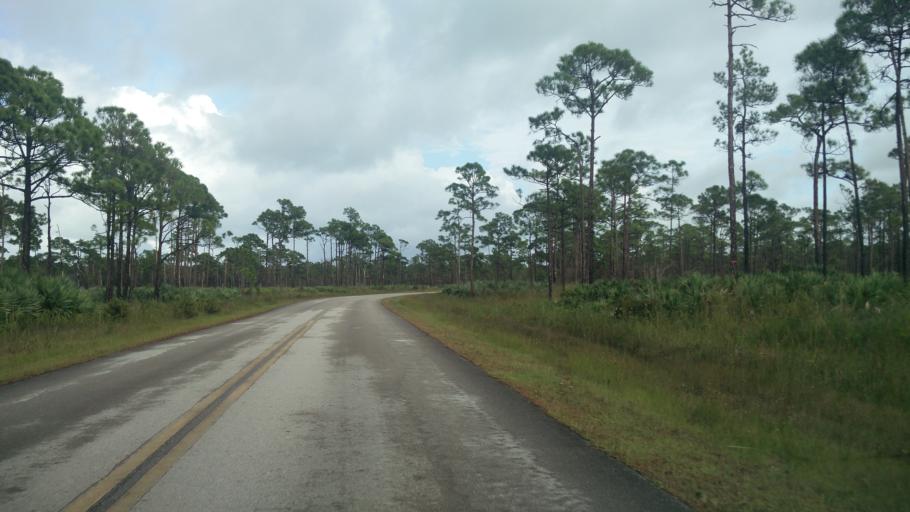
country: US
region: Florida
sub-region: Palm Beach County
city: Tequesta
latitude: 27.0076
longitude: -80.1343
